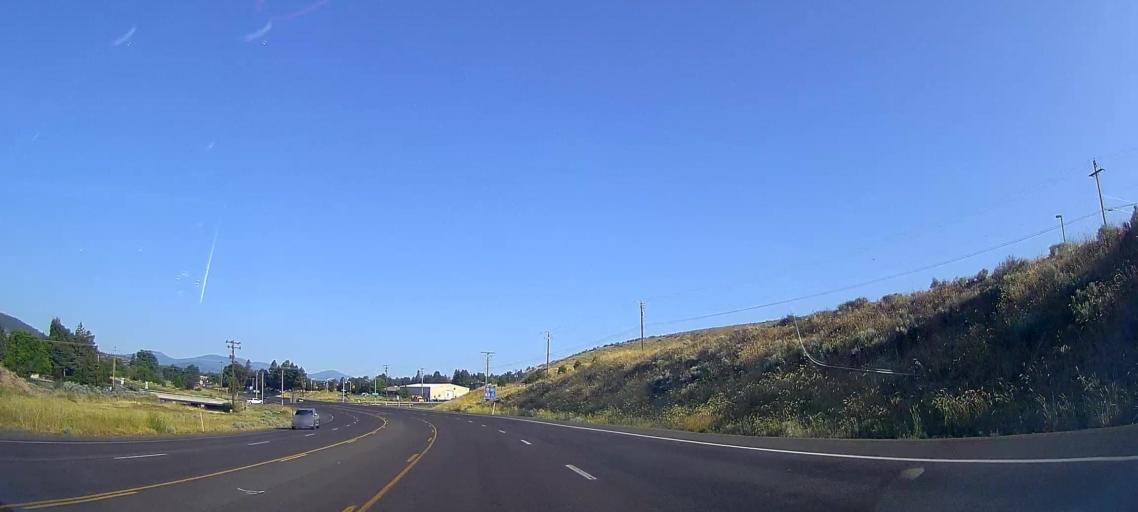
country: US
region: Oregon
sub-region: Klamath County
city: Altamont
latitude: 42.2239
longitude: -121.7547
